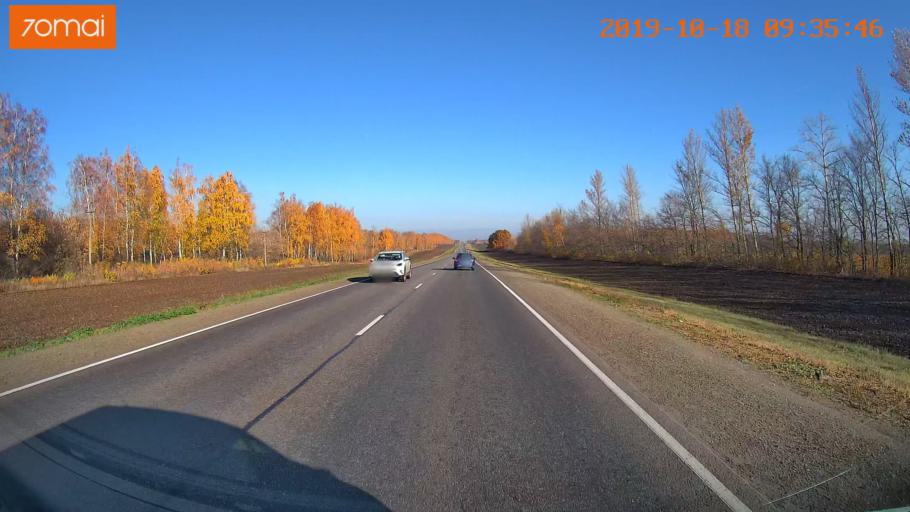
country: RU
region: Tula
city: Yefremov
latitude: 53.1966
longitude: 38.1475
